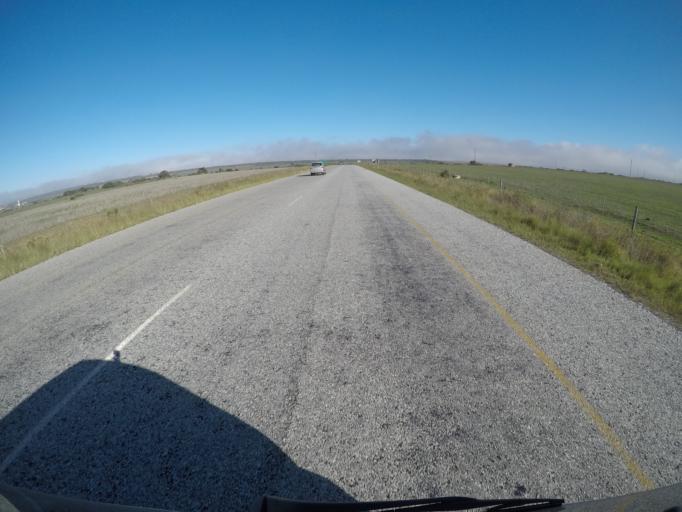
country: ZA
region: Western Cape
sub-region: Eden District Municipality
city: Mossel Bay
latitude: -34.1782
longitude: 22.0167
